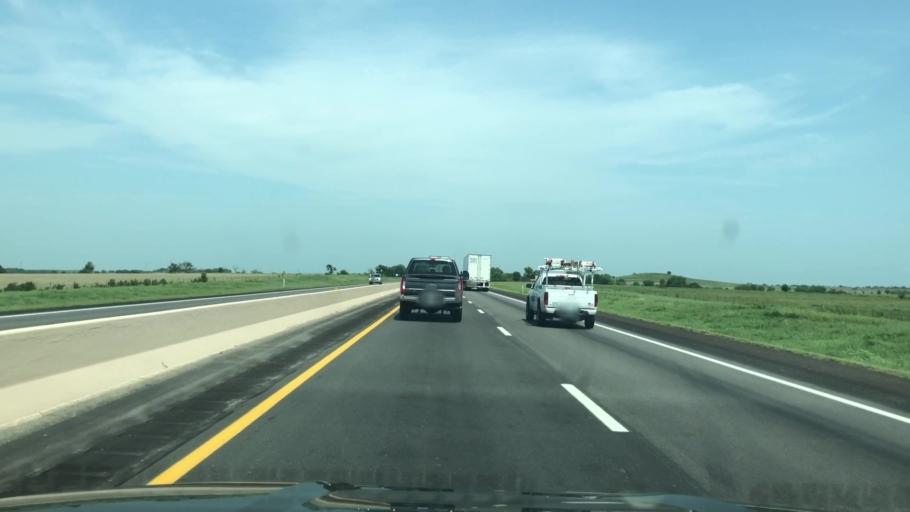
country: US
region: Oklahoma
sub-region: Ottawa County
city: Afton
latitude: 36.6801
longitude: -95.0440
